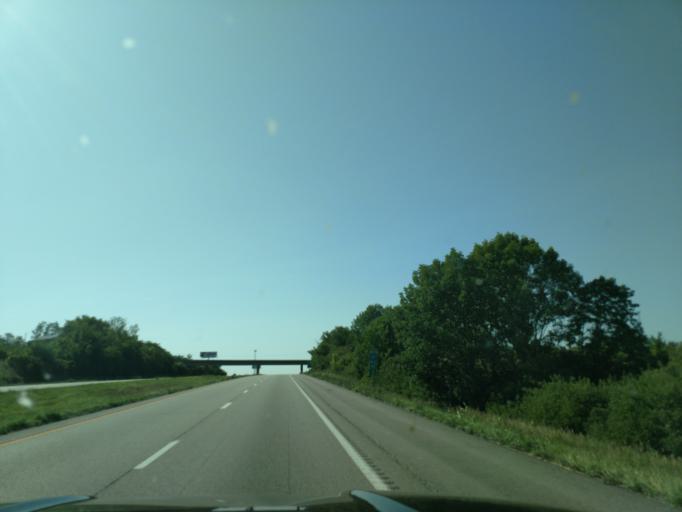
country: US
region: Missouri
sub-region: Andrew County
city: Savannah
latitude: 39.9145
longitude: -94.9021
